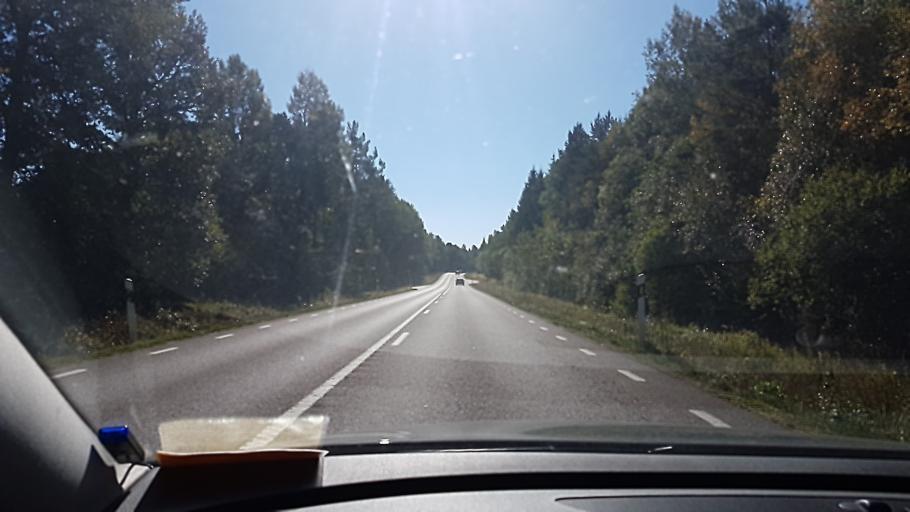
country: SE
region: Kronoberg
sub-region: Lessebo Kommun
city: Lessebo
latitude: 56.7741
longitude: 15.2563
